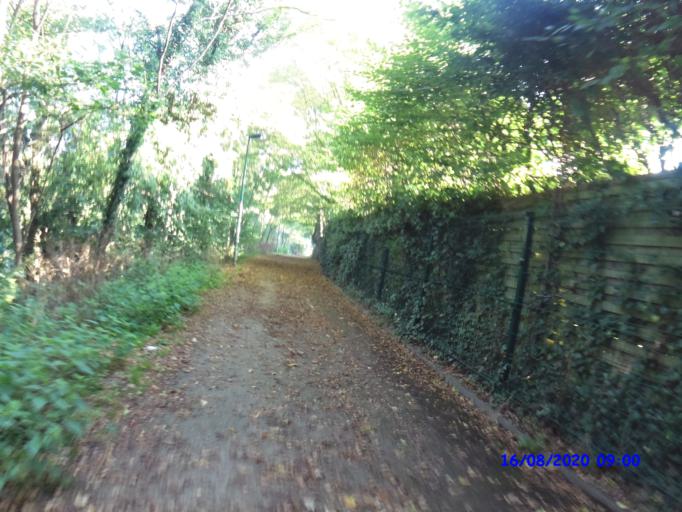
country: BE
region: Flanders
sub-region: Provincie Vlaams-Brabant
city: Linkebeek
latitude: 50.7782
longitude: 4.3359
